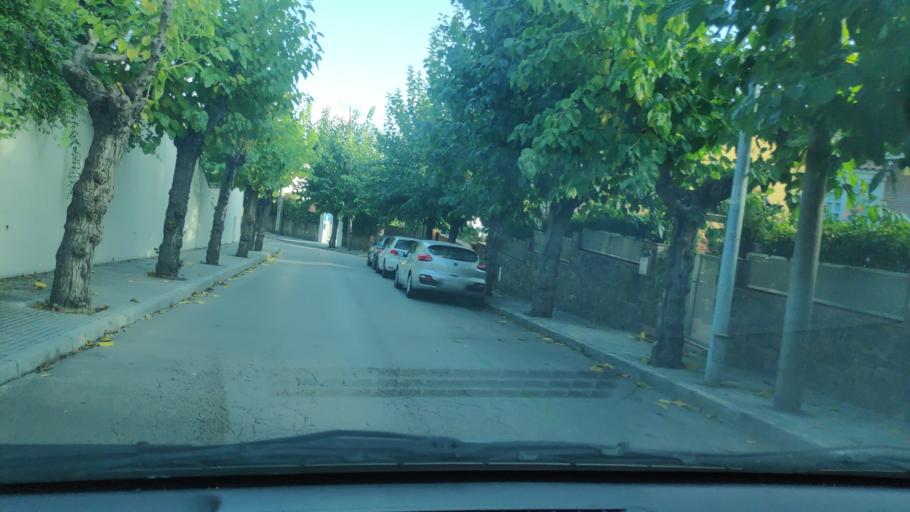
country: ES
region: Catalonia
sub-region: Provincia de Barcelona
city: Sant Quirze del Valles
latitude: 41.5017
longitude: 2.0869
